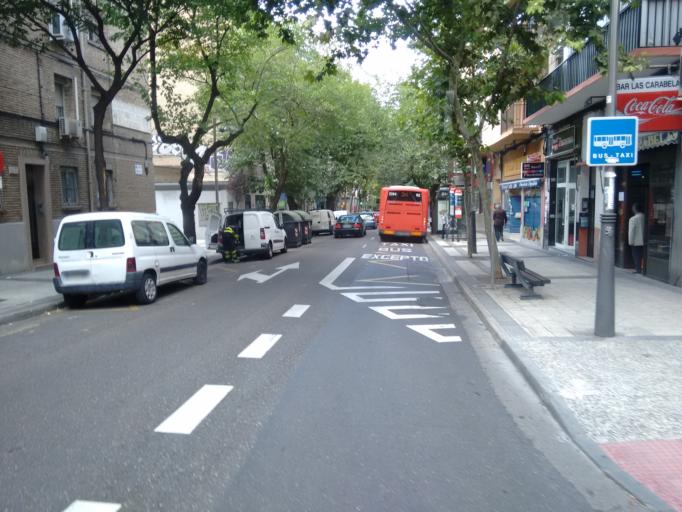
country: ES
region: Aragon
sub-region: Provincia de Zaragoza
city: Zaragoza
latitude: 41.6283
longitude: -0.8862
